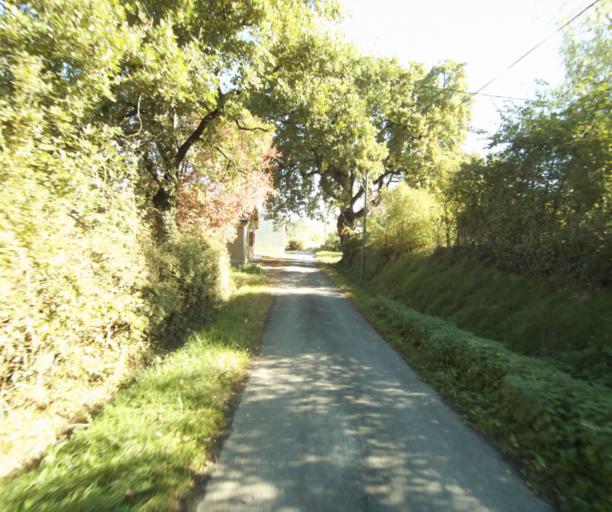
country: FR
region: Midi-Pyrenees
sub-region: Departement du Gers
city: Gondrin
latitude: 43.8184
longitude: 0.2106
